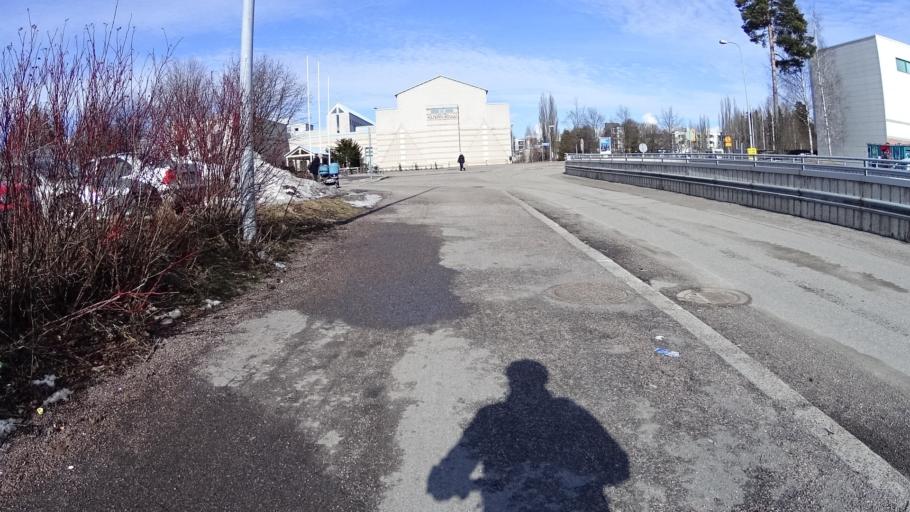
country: FI
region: Uusimaa
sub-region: Helsinki
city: Teekkarikylae
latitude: 60.2604
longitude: 24.8510
